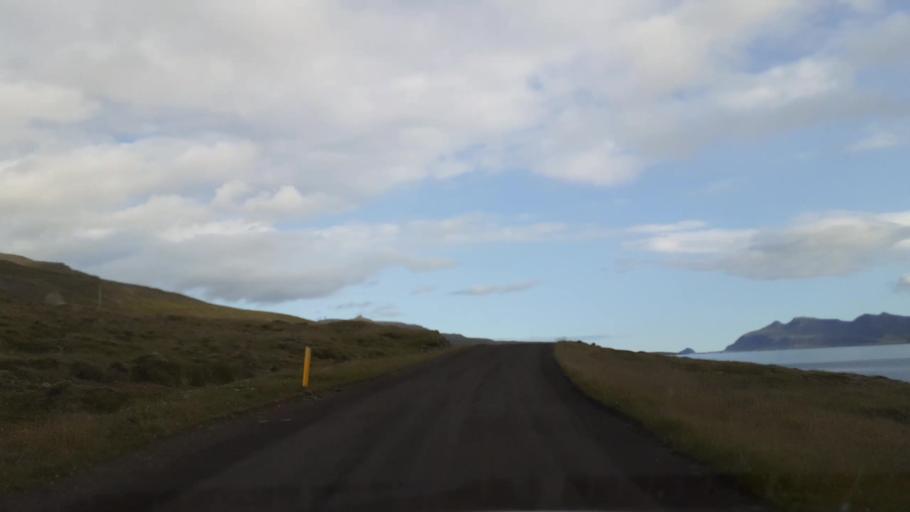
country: IS
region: East
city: Eskifjoerdur
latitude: 65.0399
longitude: -13.8871
